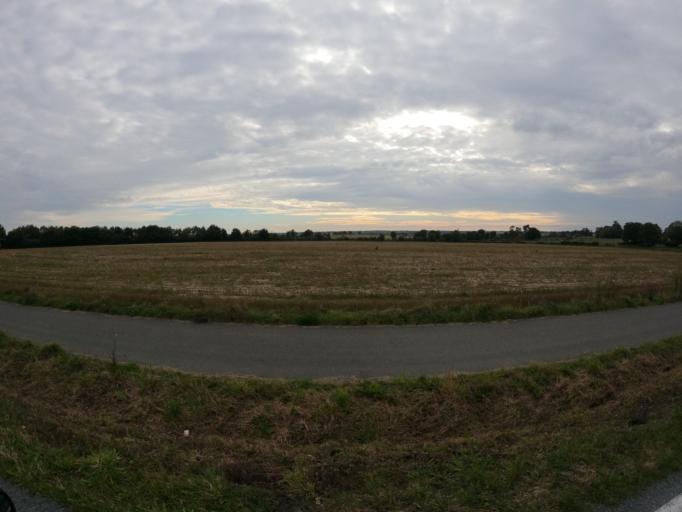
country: FR
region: Pays de la Loire
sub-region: Departement de Maine-et-Loire
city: Torfou
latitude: 47.0353
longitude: -1.1077
